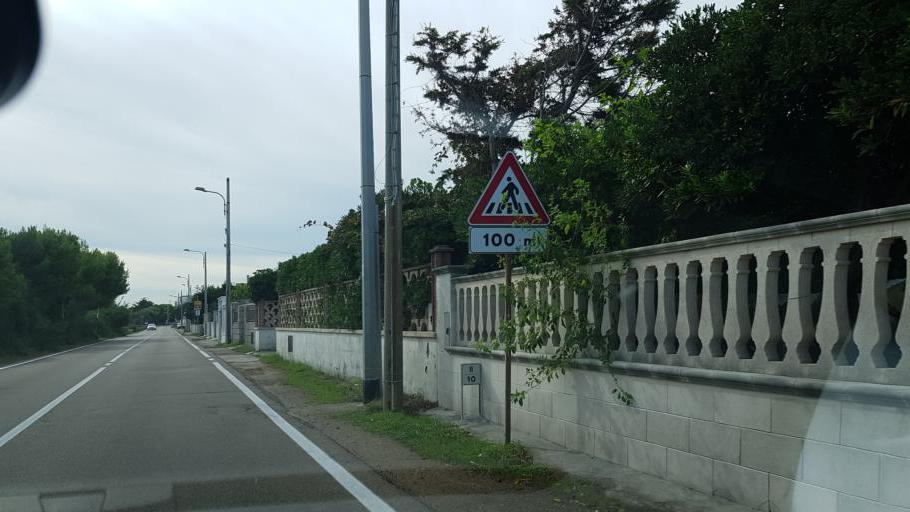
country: IT
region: Apulia
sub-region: Provincia di Lecce
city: Melendugno
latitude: 40.3262
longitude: 18.3755
